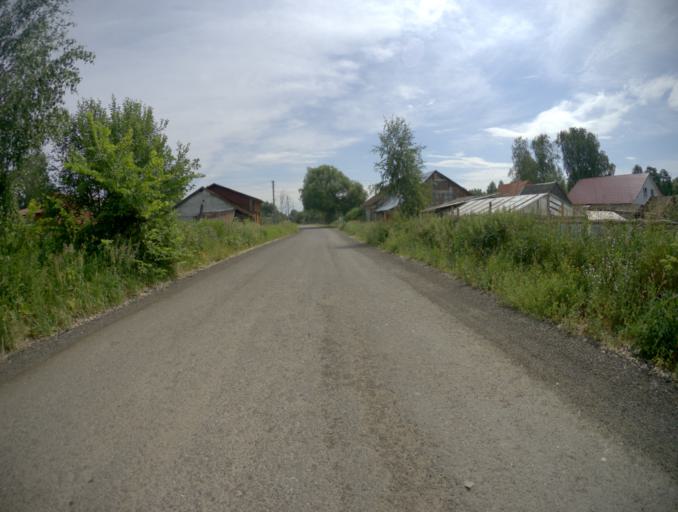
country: RU
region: Vladimir
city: Raduzhnyy
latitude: 56.0254
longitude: 40.3115
